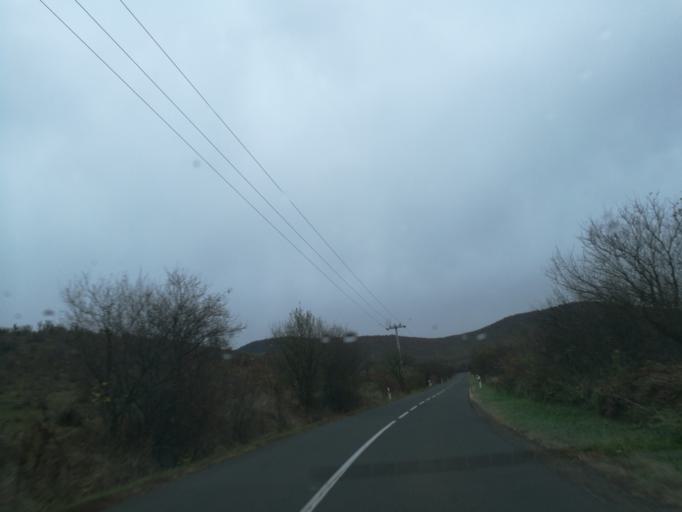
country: HU
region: Nograd
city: Rimoc
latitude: 48.0056
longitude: 19.6135
